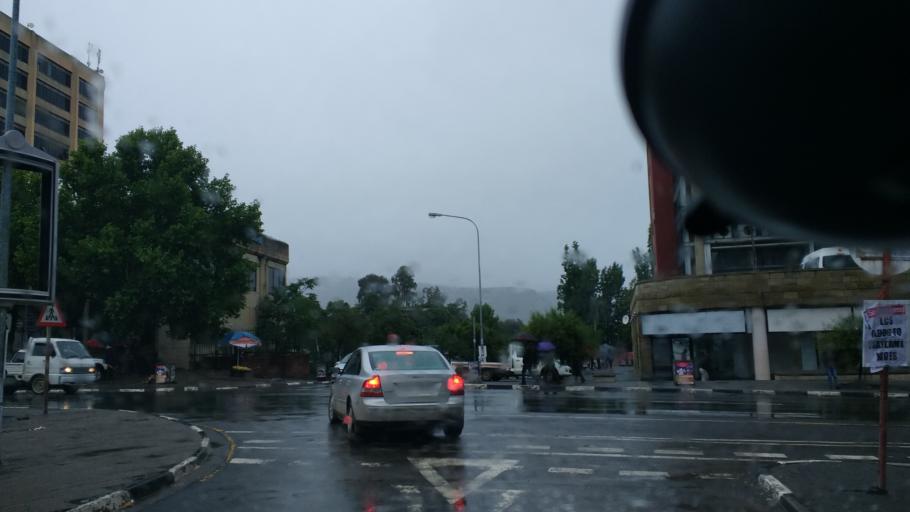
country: LS
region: Maseru
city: Maseru
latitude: -29.3139
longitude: 27.4825
